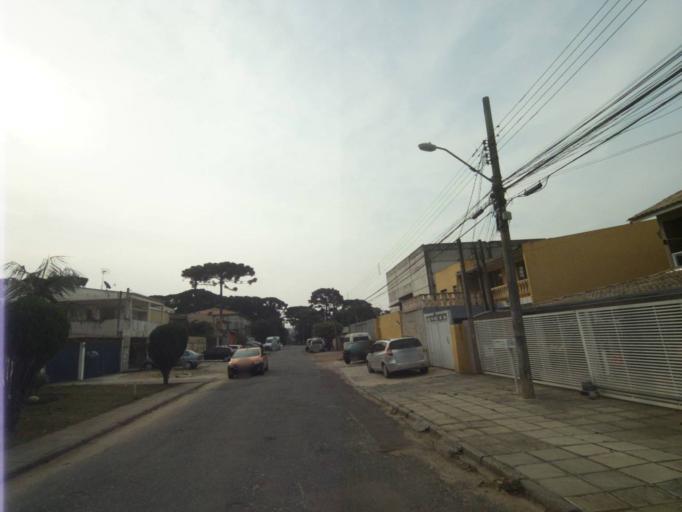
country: BR
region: Parana
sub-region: Sao Jose Dos Pinhais
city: Sao Jose dos Pinhais
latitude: -25.5267
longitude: -49.2733
